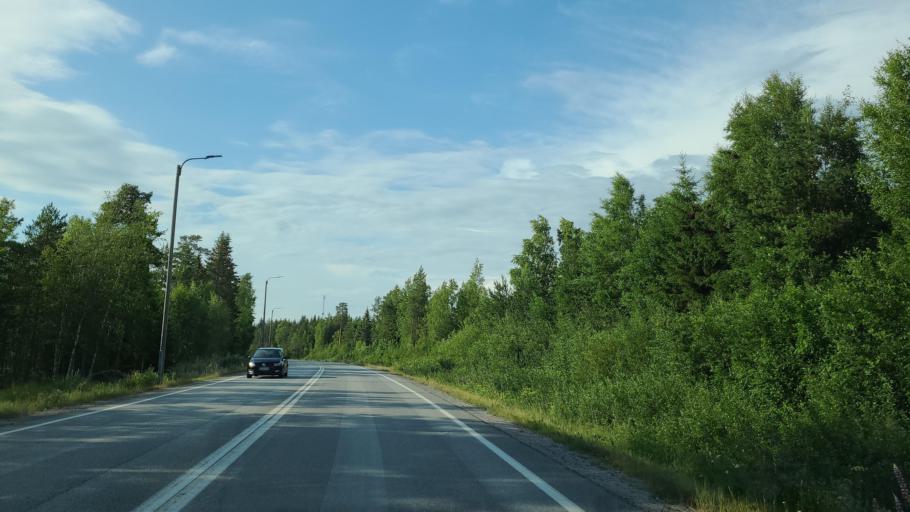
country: FI
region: Ostrobothnia
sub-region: Vaasa
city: Vaasa
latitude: 63.1373
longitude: 21.6121
